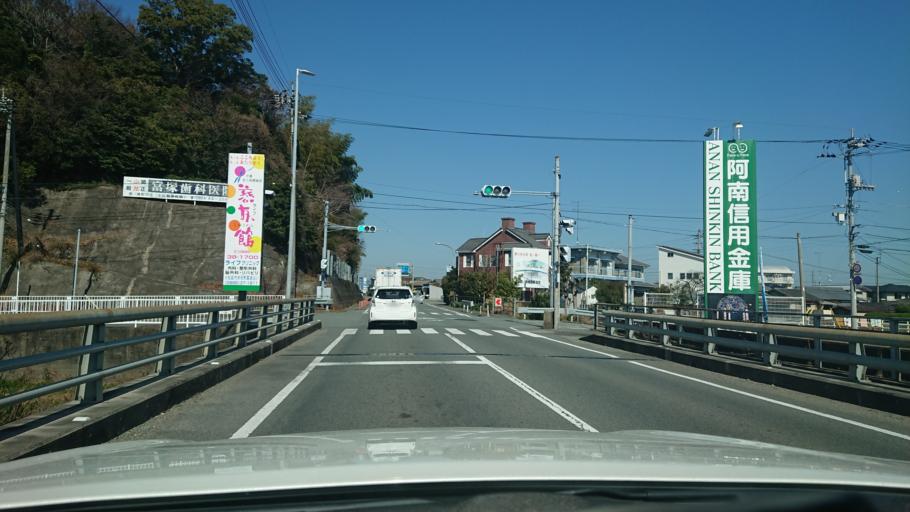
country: JP
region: Tokushima
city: Anan
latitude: 33.9552
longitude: 134.6254
